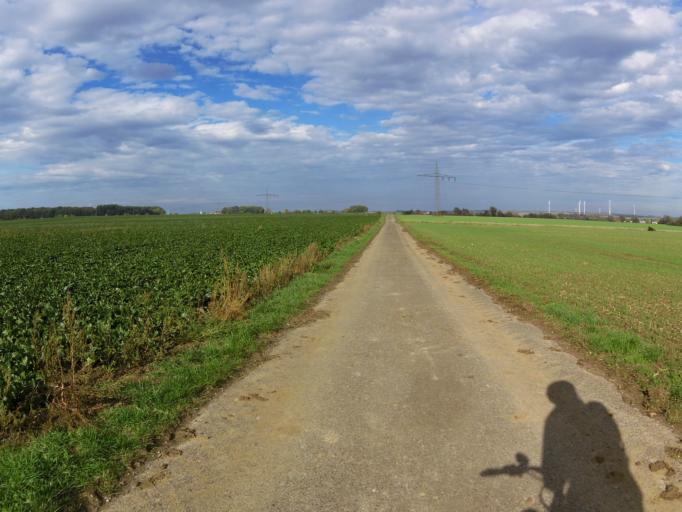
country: DE
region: Bavaria
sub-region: Regierungsbezirk Unterfranken
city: Biebelried
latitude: 49.7199
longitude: 10.0761
